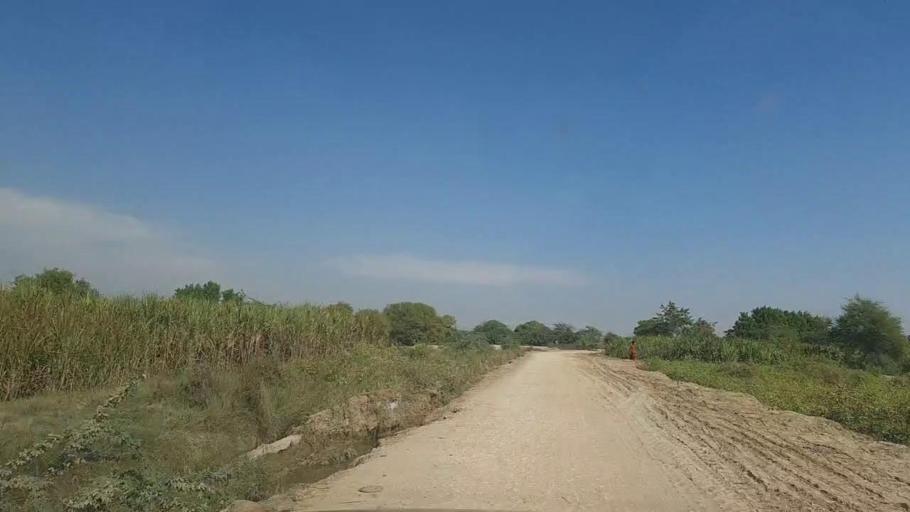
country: PK
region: Sindh
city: Mirpur Batoro
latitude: 24.7513
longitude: 68.2855
